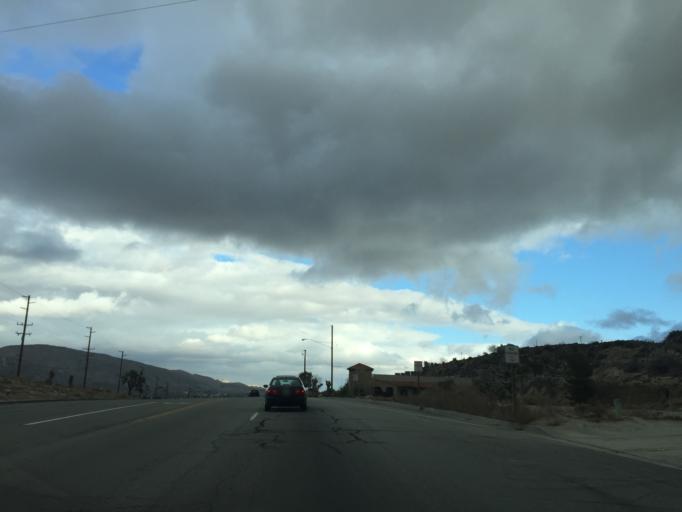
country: US
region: California
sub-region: San Bernardino County
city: Yucca Valley
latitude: 34.1099
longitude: -116.4787
